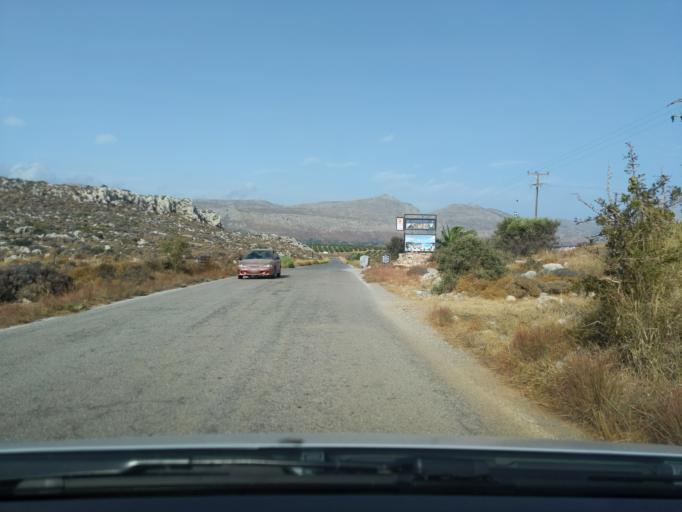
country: GR
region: Crete
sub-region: Nomos Lasithiou
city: Palekastro
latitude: 35.0855
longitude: 26.2519
